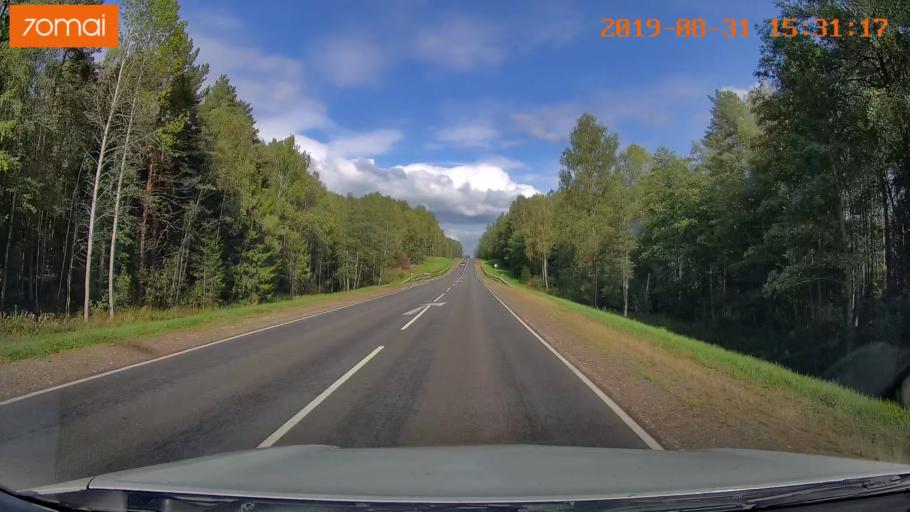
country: RU
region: Kaluga
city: Baryatino
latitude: 54.5815
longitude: 34.6512
